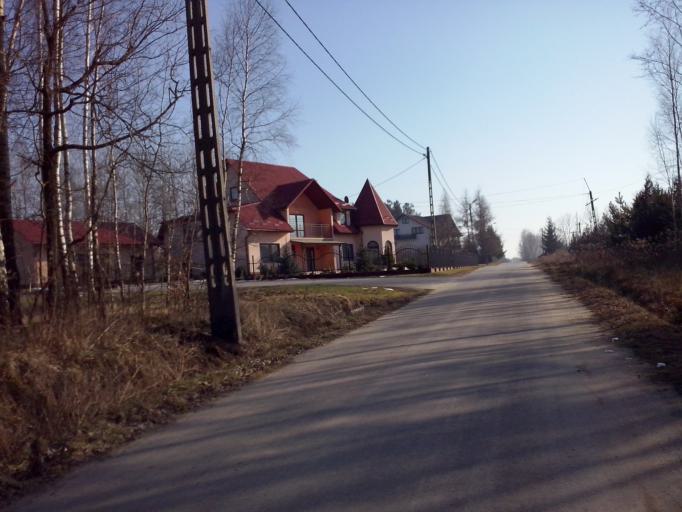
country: PL
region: Subcarpathian Voivodeship
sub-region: Powiat nizanski
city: Krzeszow
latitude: 50.4208
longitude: 22.3459
